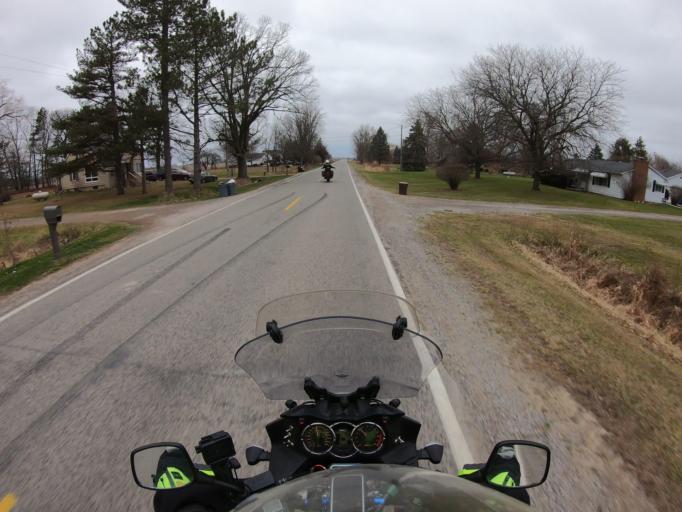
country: US
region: Michigan
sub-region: Saginaw County
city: Burt
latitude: 43.2415
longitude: -83.9865
